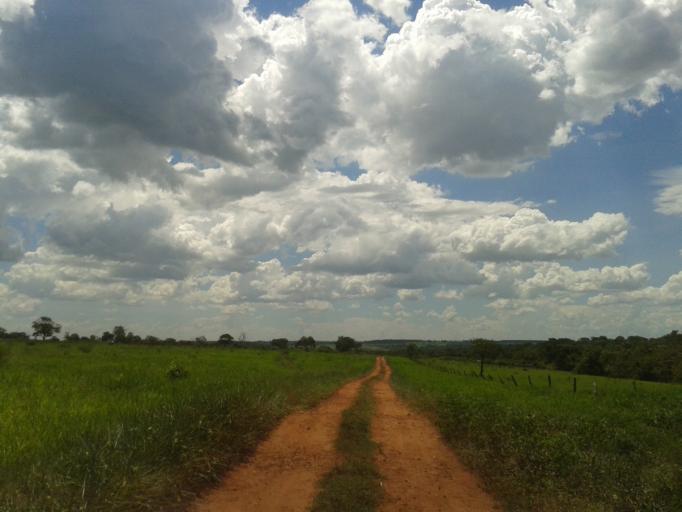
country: BR
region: Minas Gerais
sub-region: Santa Vitoria
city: Santa Vitoria
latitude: -19.1139
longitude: -50.5178
